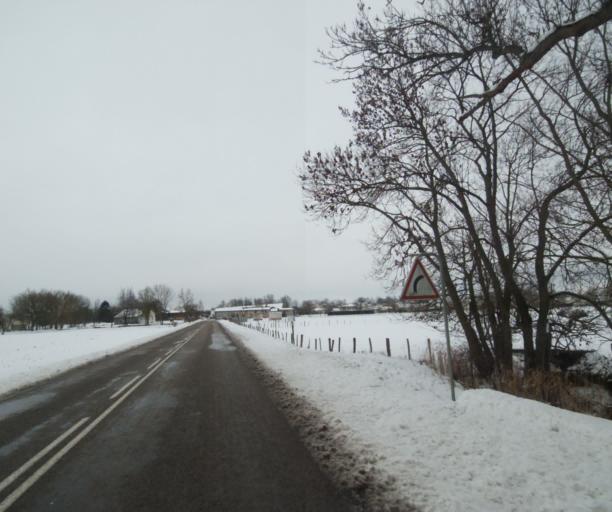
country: FR
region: Champagne-Ardenne
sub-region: Departement de la Haute-Marne
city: Montier-en-Der
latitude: 48.4758
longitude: 4.7860
